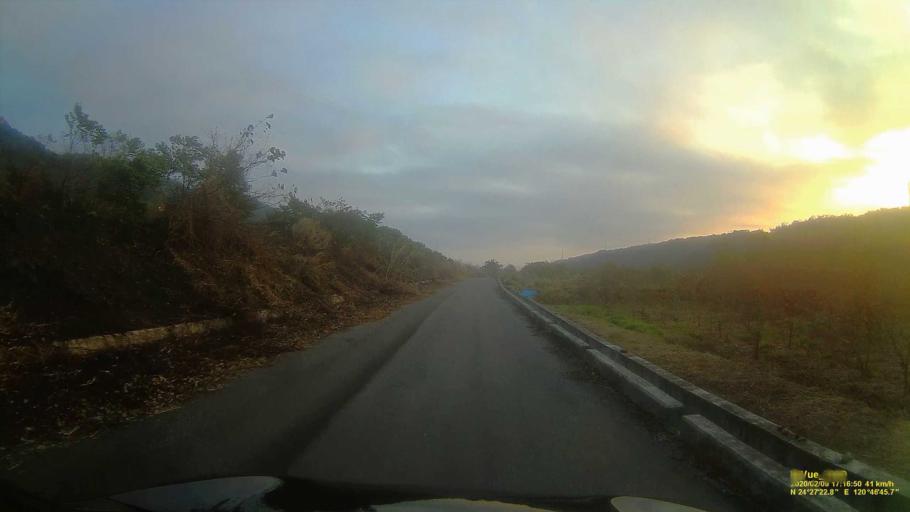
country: TW
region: Taiwan
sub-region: Miaoli
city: Miaoli
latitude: 24.4560
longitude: 120.7794
